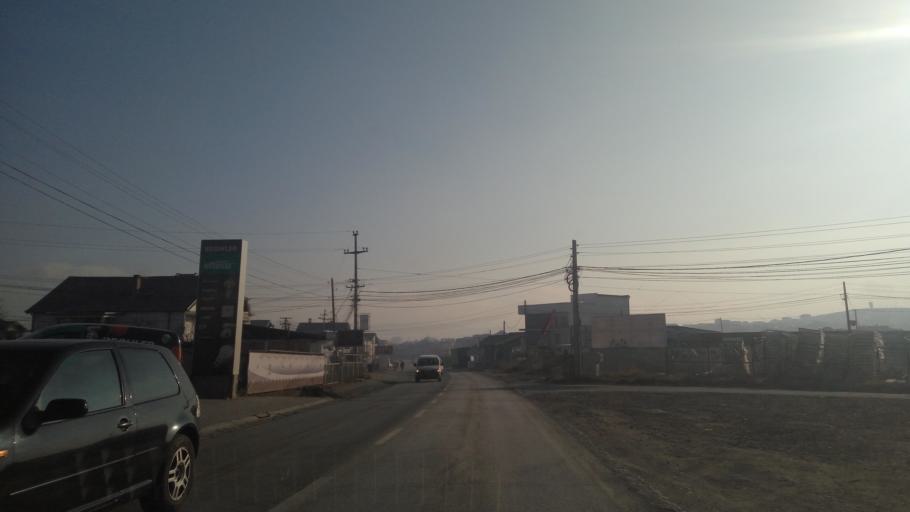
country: XK
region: Gjilan
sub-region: Komuna e Gjilanit
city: Gjilan
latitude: 42.4659
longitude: 21.4485
